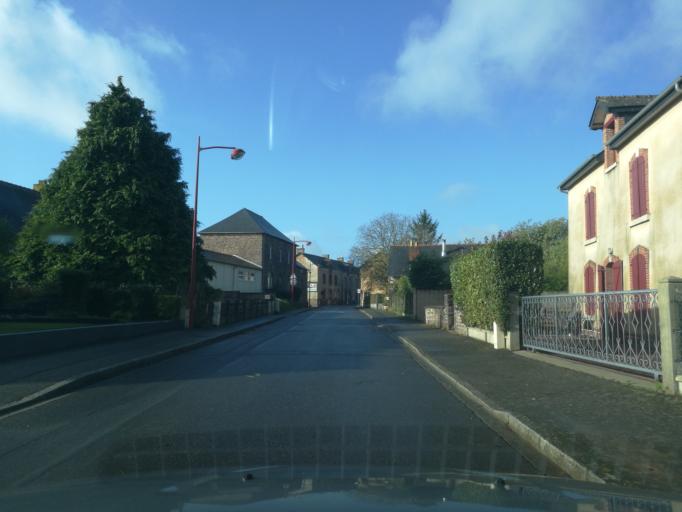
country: FR
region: Brittany
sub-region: Departement d'Ille-et-Vilaine
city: Pleumeleuc
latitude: 48.1842
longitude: -1.9159
